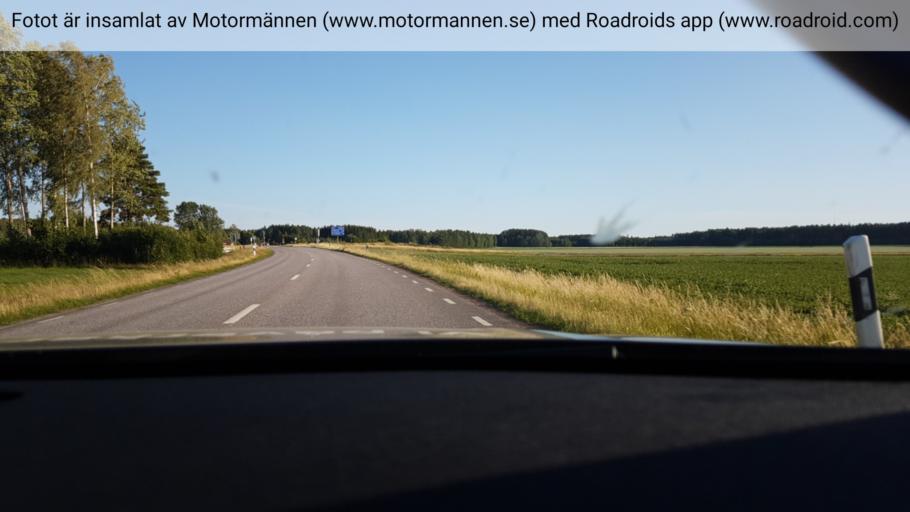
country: SE
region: Vaestra Goetaland
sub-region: Skovde Kommun
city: Stopen
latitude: 58.4770
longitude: 13.9555
